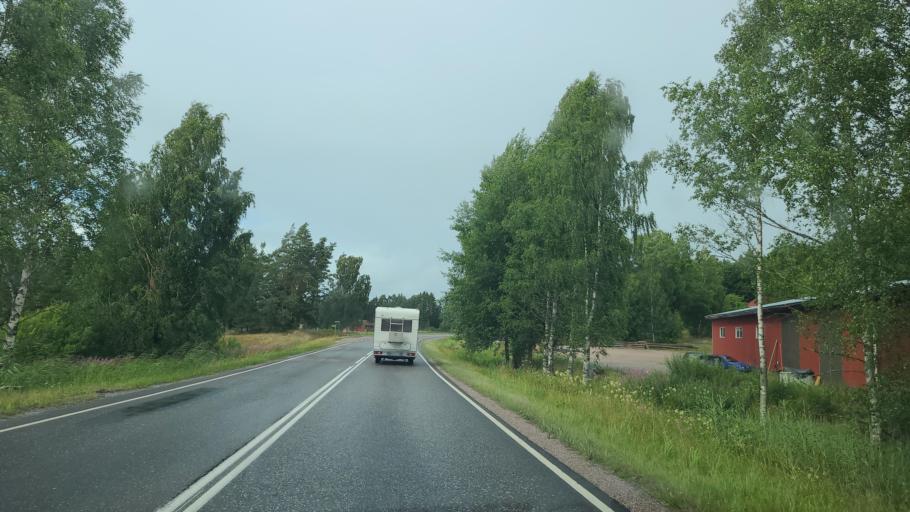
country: FI
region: Varsinais-Suomi
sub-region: Turku
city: Sauvo
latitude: 60.3077
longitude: 22.6875
